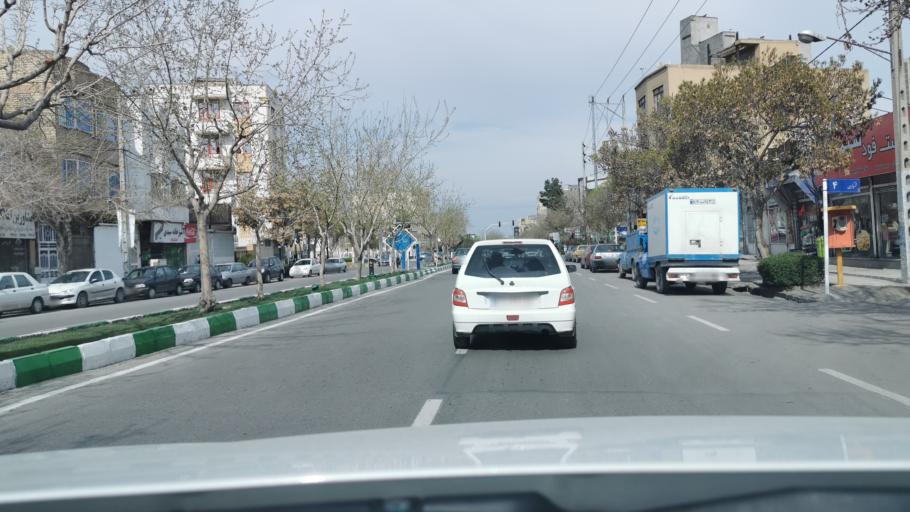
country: IR
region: Razavi Khorasan
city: Mashhad
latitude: 36.3198
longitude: 59.6029
